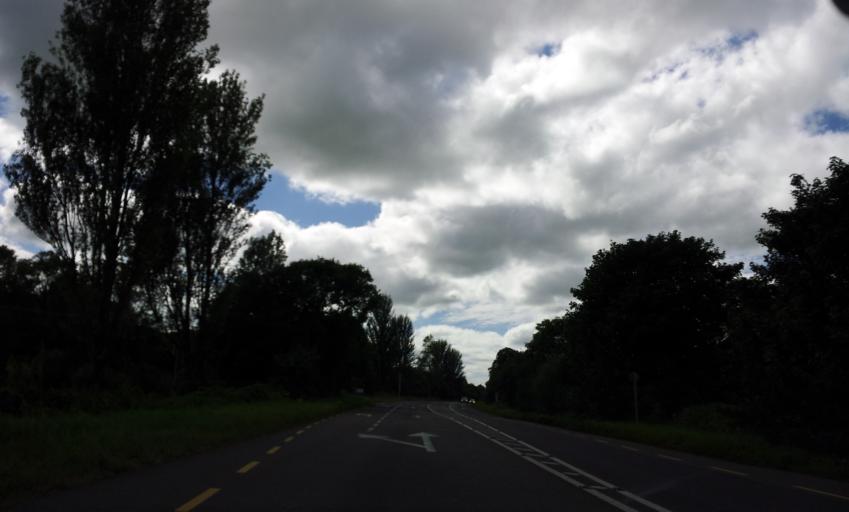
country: IE
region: Munster
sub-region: County Cork
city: Bandon
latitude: 51.8621
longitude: -8.7823
